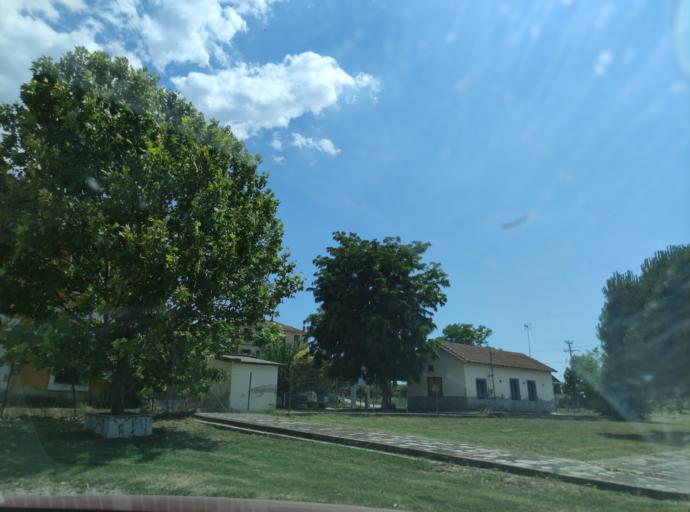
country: GR
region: Central Macedonia
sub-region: Nomos Serron
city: Alistrati
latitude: 41.0073
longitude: 23.9388
